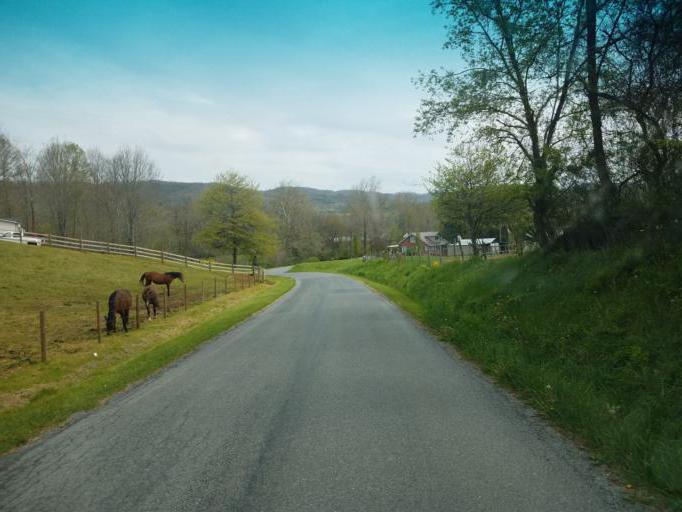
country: US
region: Virginia
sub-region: Smyth County
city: Marion
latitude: 36.7695
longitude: -81.4541
